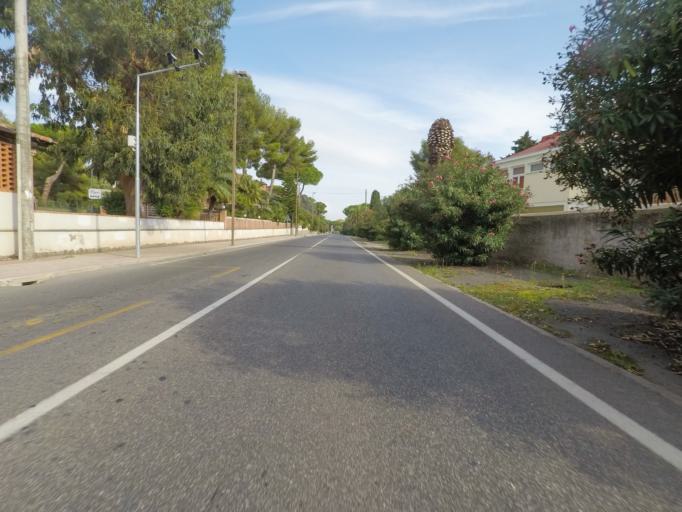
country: IT
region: Latium
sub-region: Citta metropolitana di Roma Capitale
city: Santa Marinella
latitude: 42.0323
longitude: 11.8414
